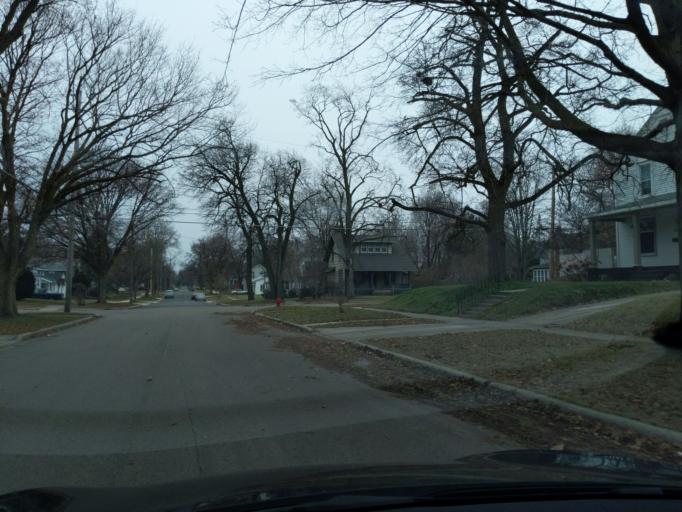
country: US
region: Michigan
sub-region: Ingham County
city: Lansing
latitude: 42.7138
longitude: -84.5580
